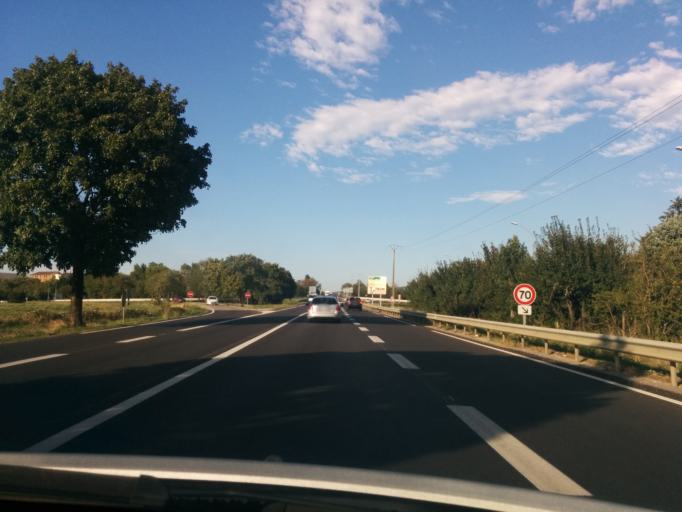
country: FR
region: Rhone-Alpes
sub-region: Departement de l'Ain
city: Amberieu-en-Bugey
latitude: 45.9694
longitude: 5.3399
